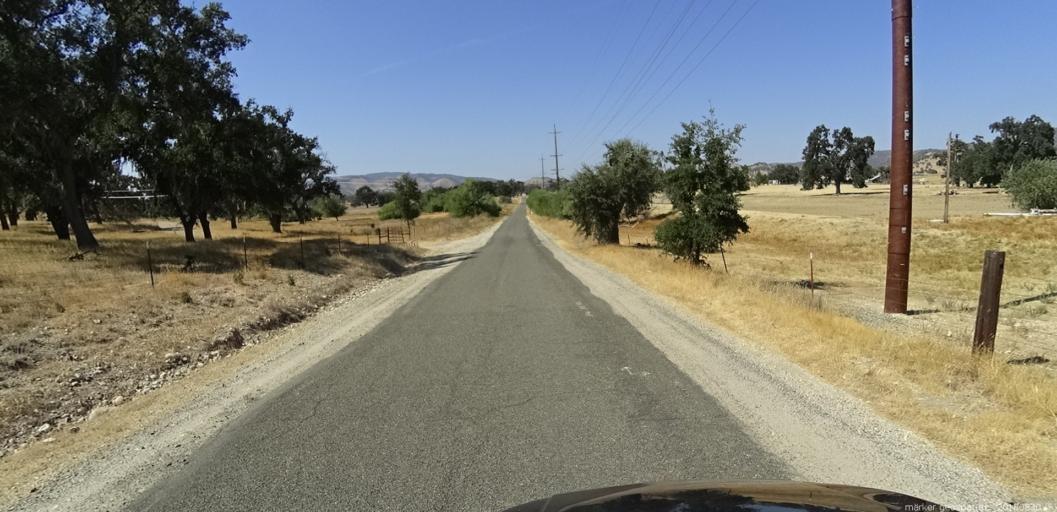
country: US
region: California
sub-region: Monterey County
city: King City
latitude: 36.0160
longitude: -121.1692
